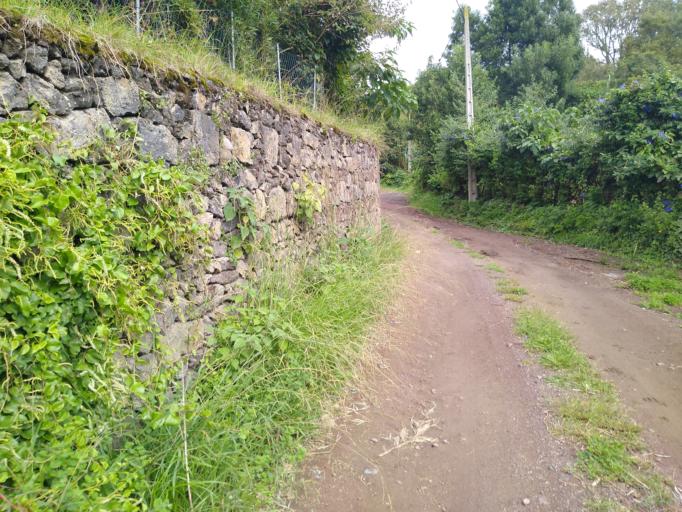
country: PT
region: Azores
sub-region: Ponta Delgada
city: Arrifes
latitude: 37.8396
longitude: -25.8251
